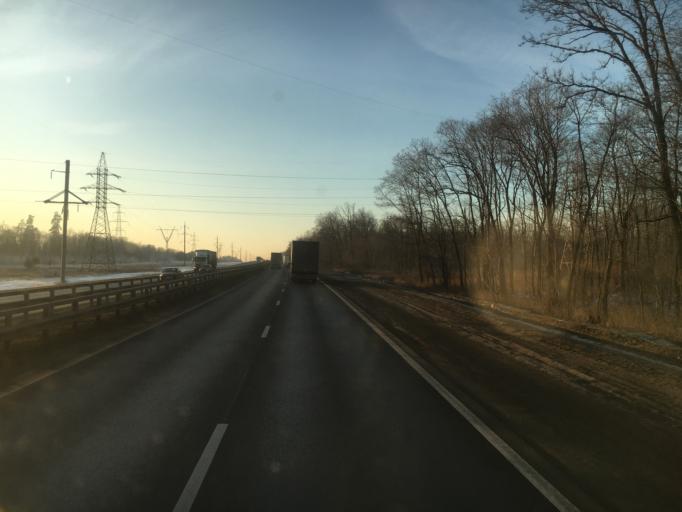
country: RU
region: Samara
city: Pribrezhnyy
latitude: 53.5187
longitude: 49.8184
